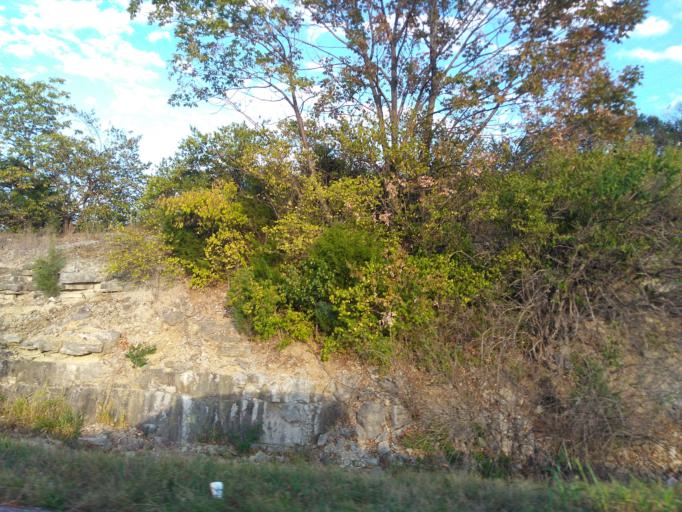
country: US
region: Missouri
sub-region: Saint Louis County
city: Sunset Hills
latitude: 38.5251
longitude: -90.3975
